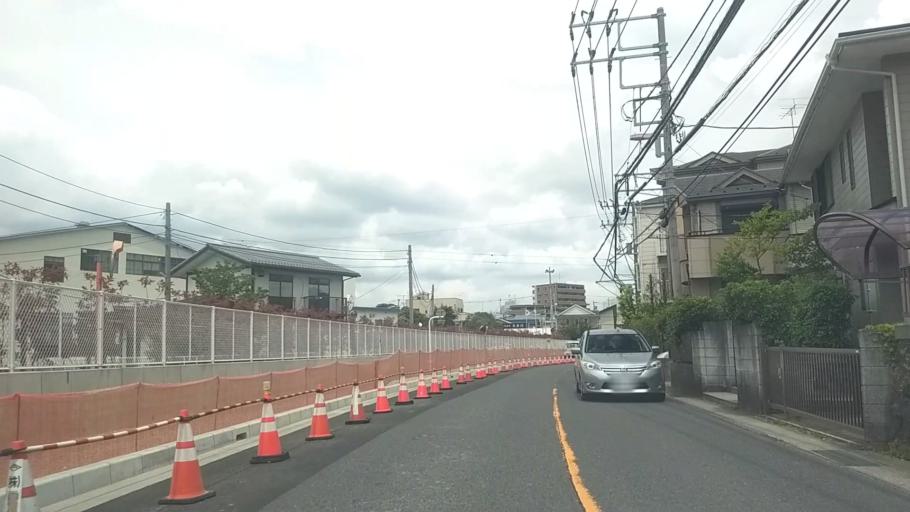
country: JP
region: Kanagawa
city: Kamakura
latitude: 35.3470
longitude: 139.5274
